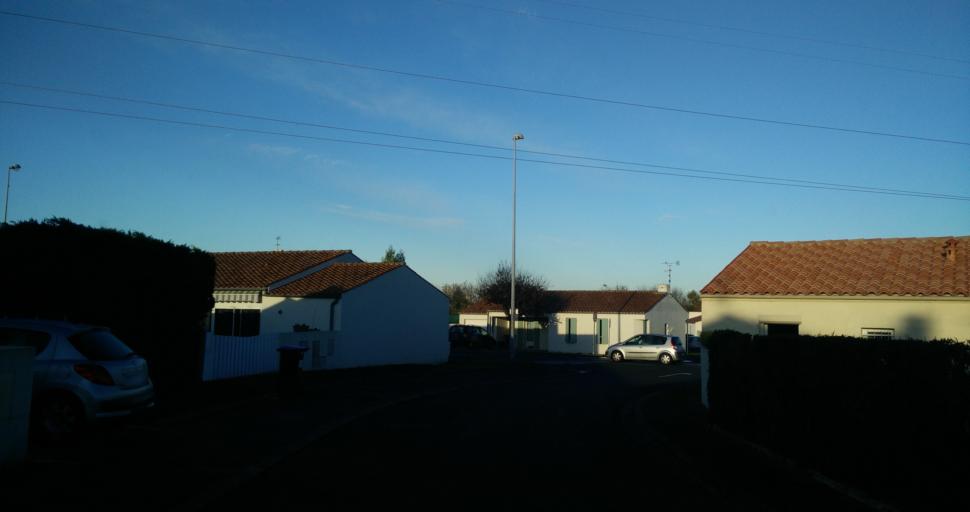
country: FR
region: Poitou-Charentes
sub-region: Departement de la Charente-Maritime
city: Puilboreau
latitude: 46.1867
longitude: -1.1240
